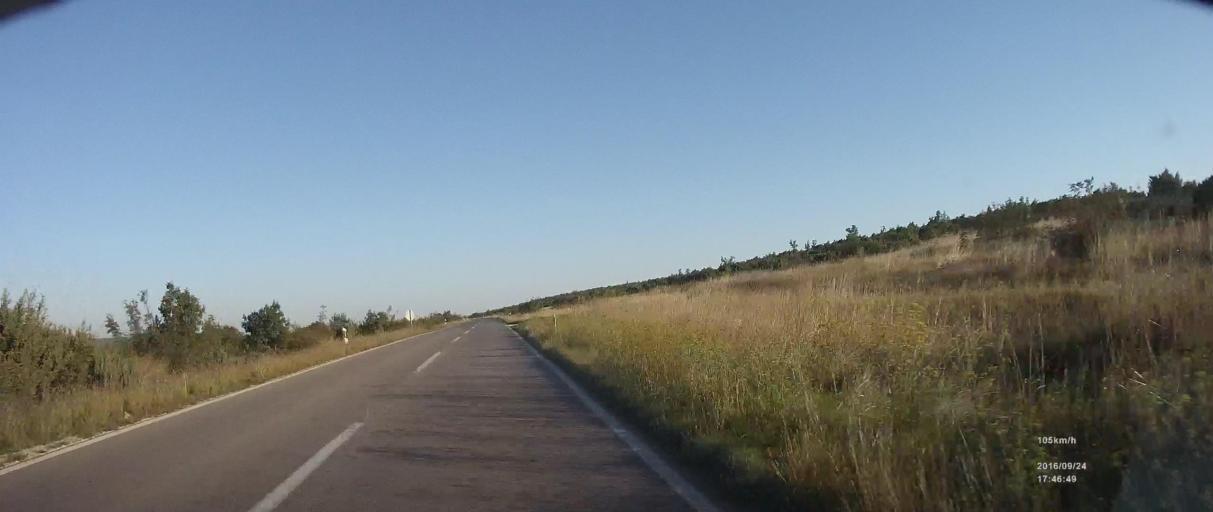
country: HR
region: Zadarska
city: Polaca
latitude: 44.0832
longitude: 15.5132
